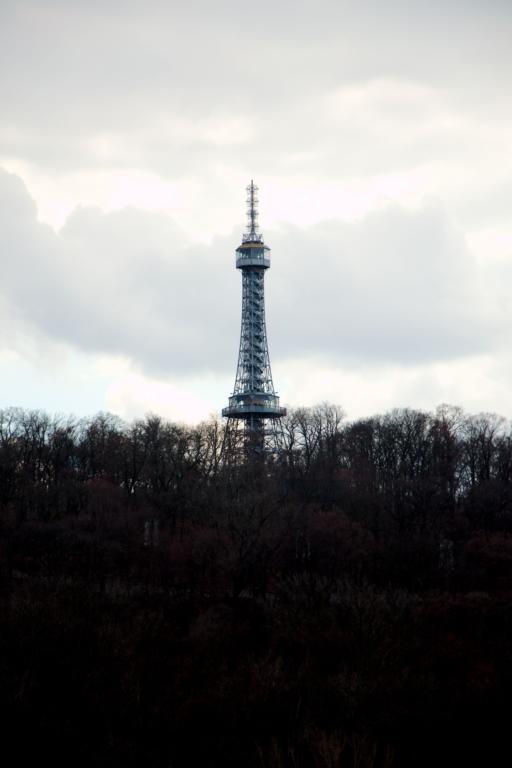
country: CZ
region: Praha
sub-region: Praha 1
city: Mala Strana
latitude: 50.0894
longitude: 14.3988
